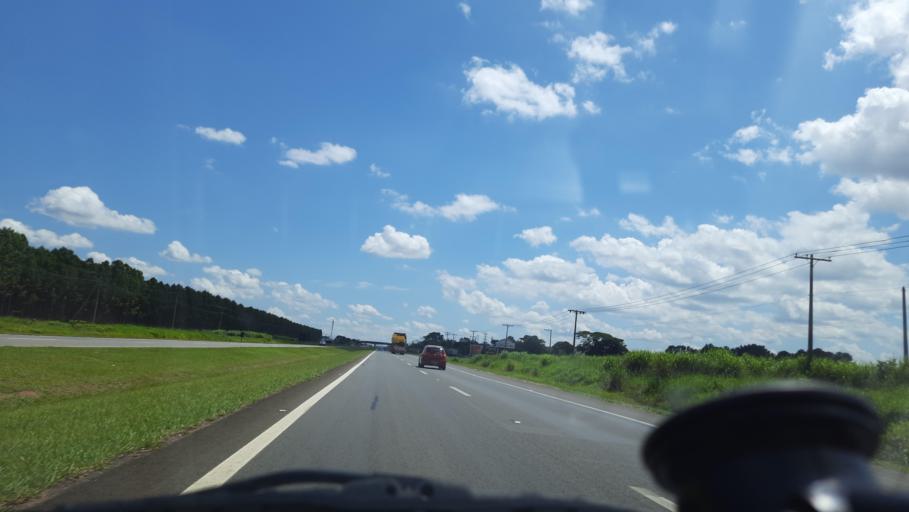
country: BR
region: Sao Paulo
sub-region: Moji-Guacu
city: Mogi-Gaucu
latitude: -22.3311
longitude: -46.9601
